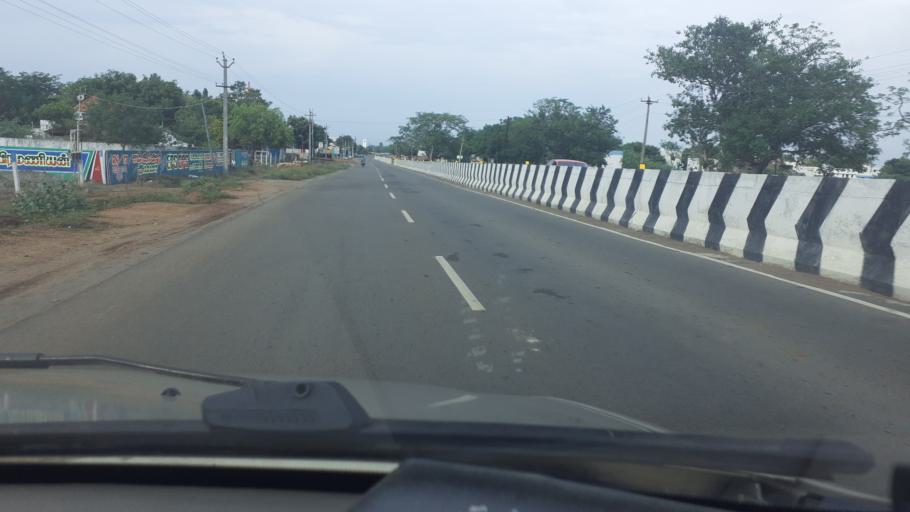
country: IN
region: Tamil Nadu
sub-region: Tirunelveli Kattabo
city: Tirunelveli
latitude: 8.6631
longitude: 77.7155
